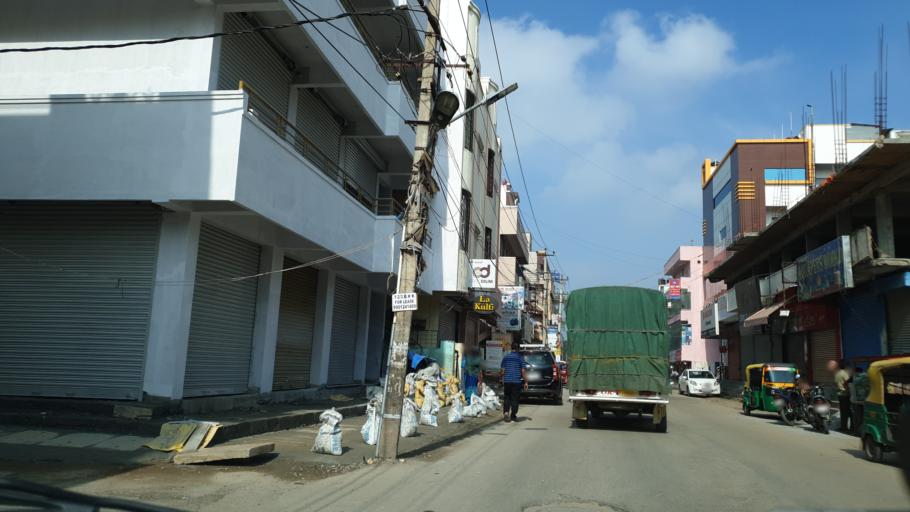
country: IN
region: Karnataka
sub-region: Bangalore Urban
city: Bangalore
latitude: 12.9725
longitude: 77.6789
